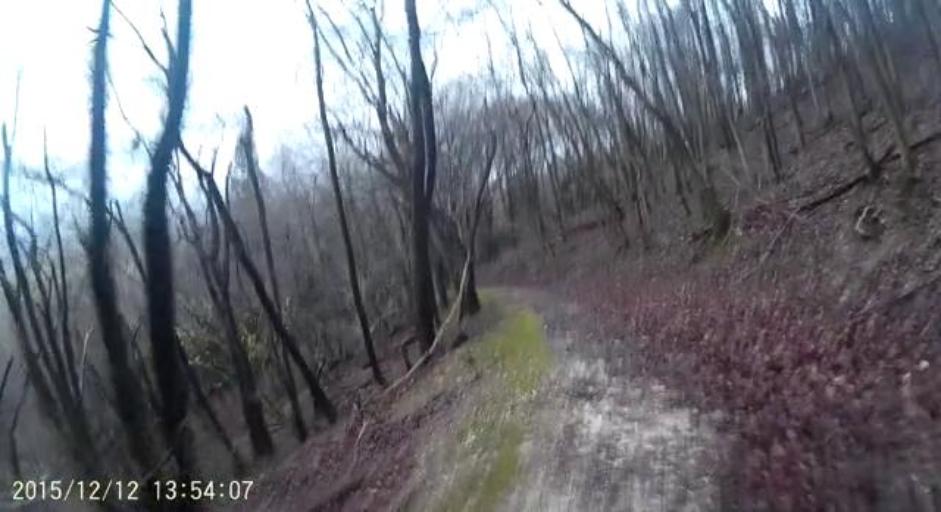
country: GB
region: England
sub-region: West Sussex
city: Milland
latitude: 50.9595
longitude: -0.8462
